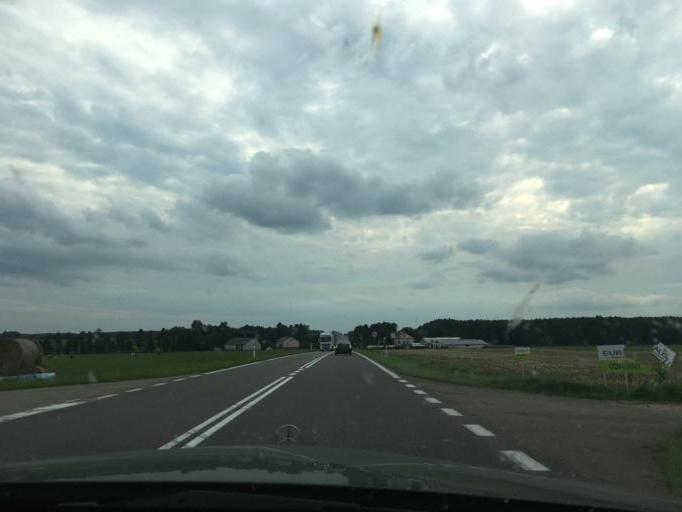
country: PL
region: Podlasie
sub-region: Powiat grajewski
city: Szczuczyn
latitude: 53.4941
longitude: 22.2266
